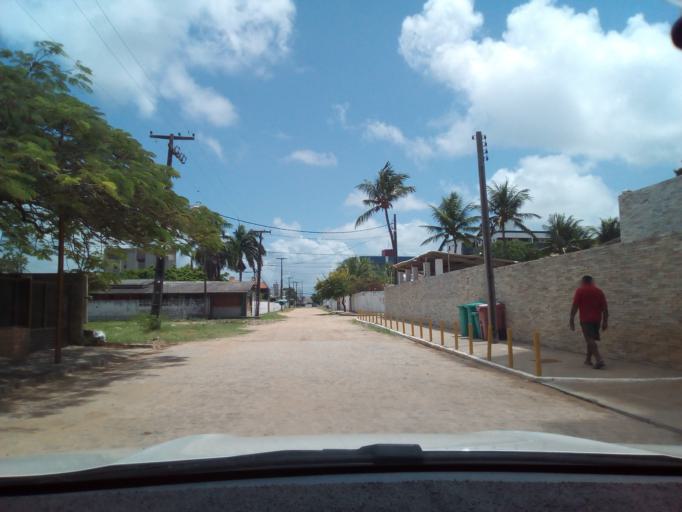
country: BR
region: Paraiba
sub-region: Cabedelo
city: Cabedelo
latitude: -7.0139
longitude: -34.8292
